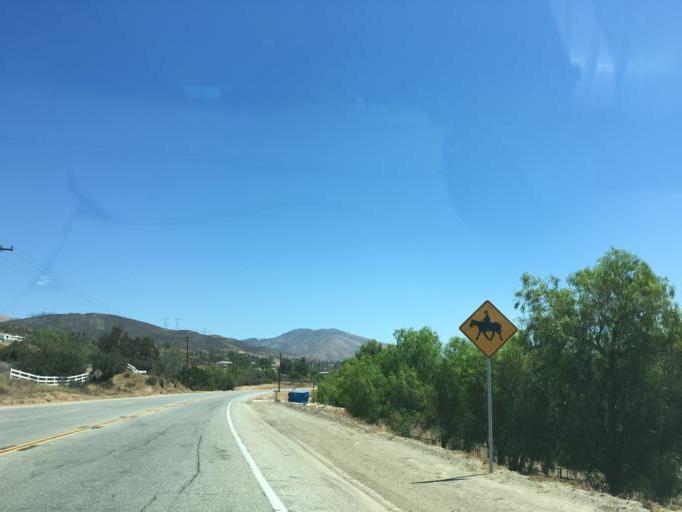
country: US
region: California
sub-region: Los Angeles County
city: Agua Dulce
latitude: 34.5192
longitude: -118.3223
